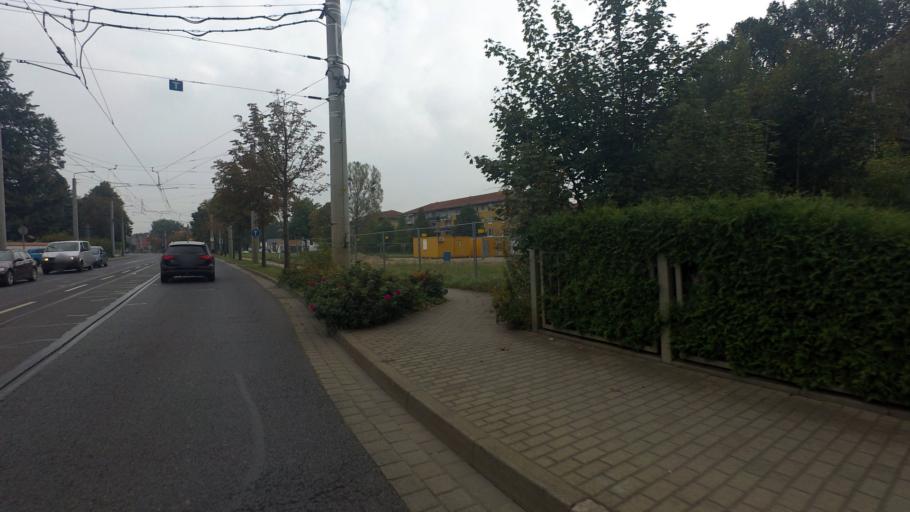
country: DE
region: Saxony
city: Albertstadt
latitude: 51.1201
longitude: 13.7905
